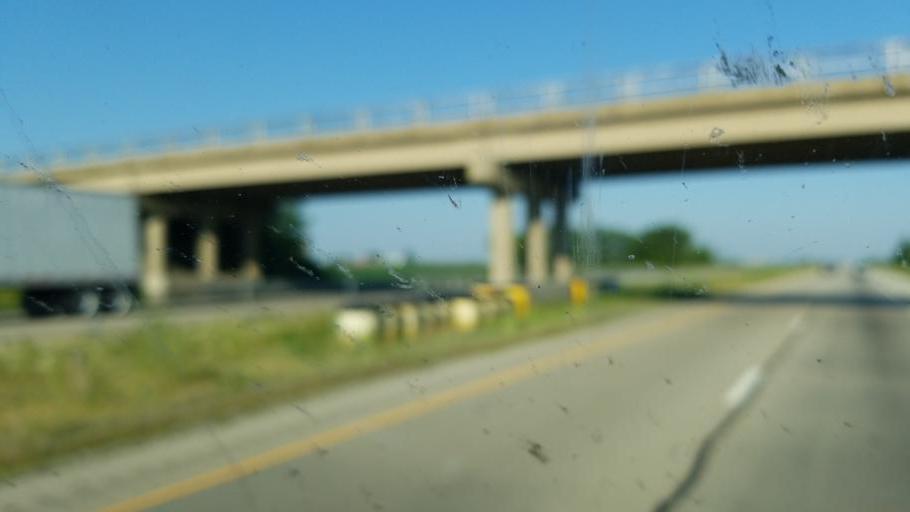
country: US
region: Illinois
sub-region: LaSalle County
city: Seneca
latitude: 41.3761
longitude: -88.6322
